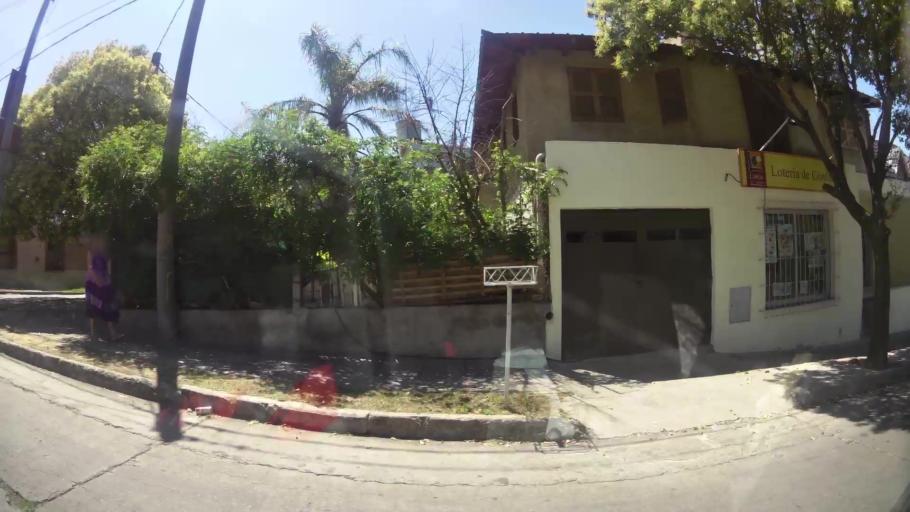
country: AR
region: Cordoba
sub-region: Departamento de Capital
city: Cordoba
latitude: -31.4329
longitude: -64.2096
